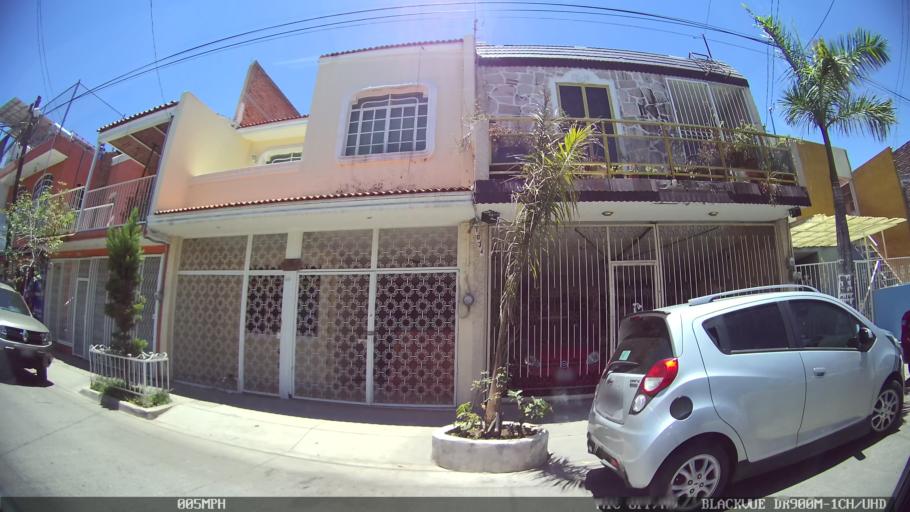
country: MX
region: Jalisco
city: Tlaquepaque
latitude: 20.6776
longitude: -103.2911
